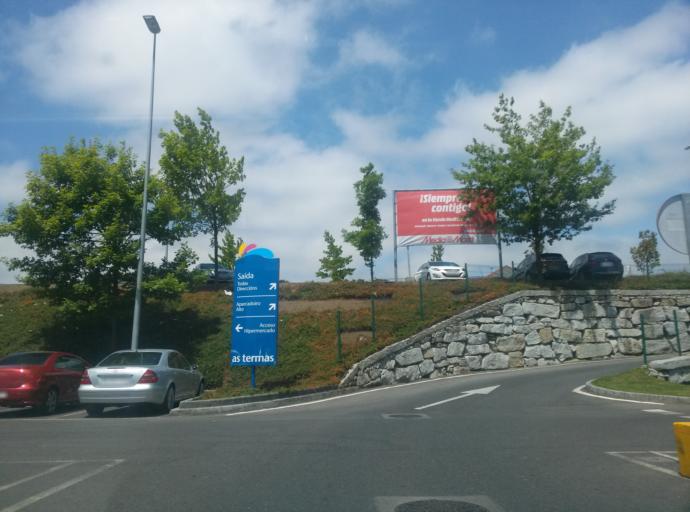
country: ES
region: Galicia
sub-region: Provincia de Lugo
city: Lugo
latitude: 43.0374
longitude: -7.5679
